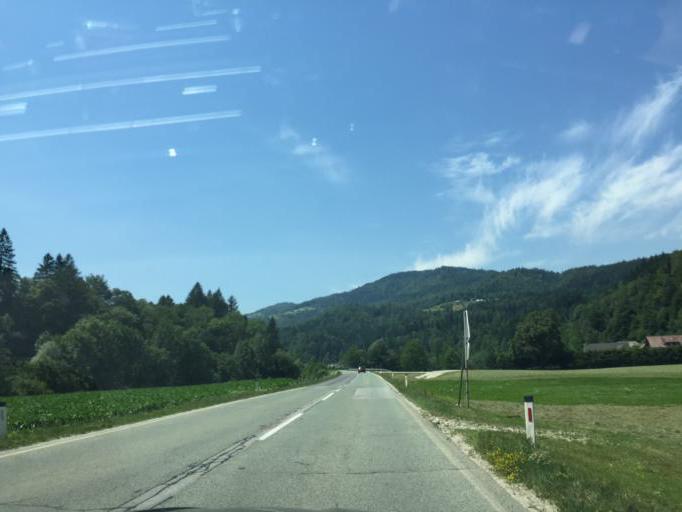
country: SI
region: Skofja Loka
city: Skofja Loka
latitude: 46.1396
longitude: 14.2647
